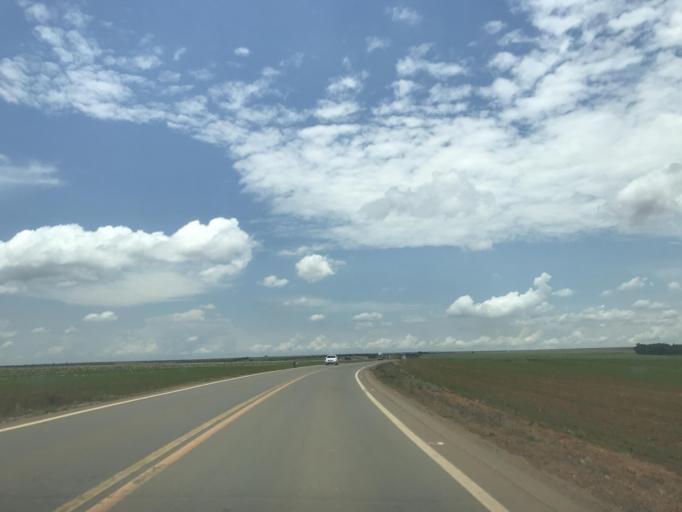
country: BR
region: Goias
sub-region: Luziania
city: Luziania
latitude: -16.4973
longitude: -48.2027
